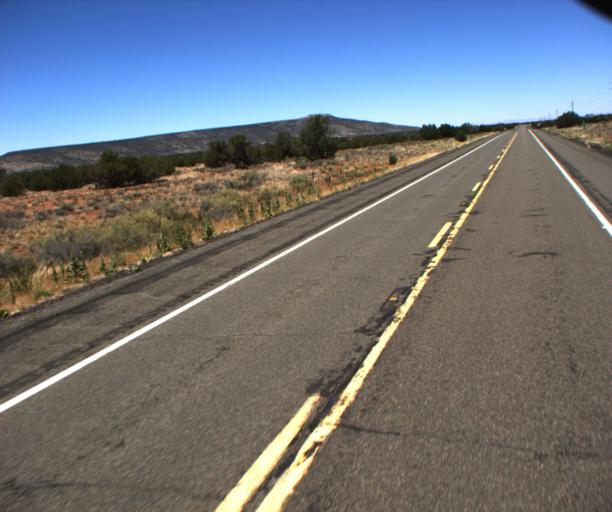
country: US
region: Arizona
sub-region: Coconino County
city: LeChee
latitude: 34.8170
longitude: -110.9653
